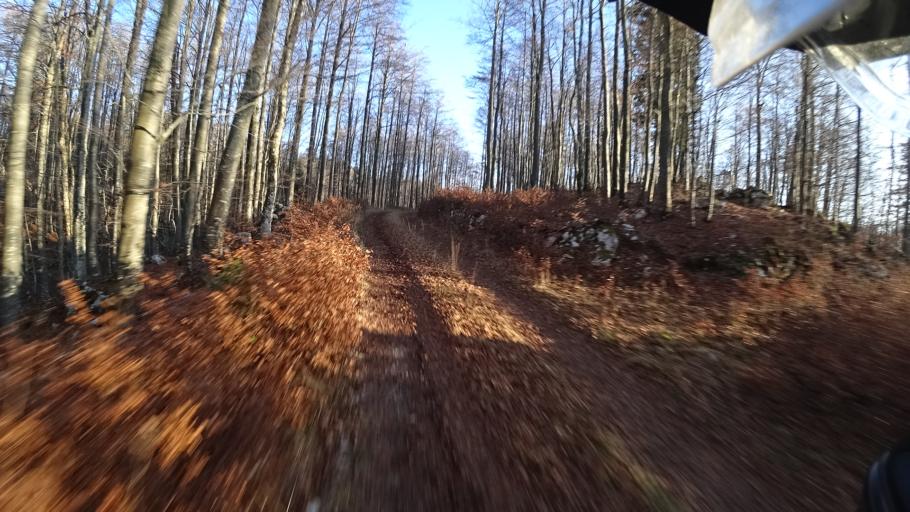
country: HR
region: Primorsko-Goranska
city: Drazice
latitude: 45.4980
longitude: 14.4834
